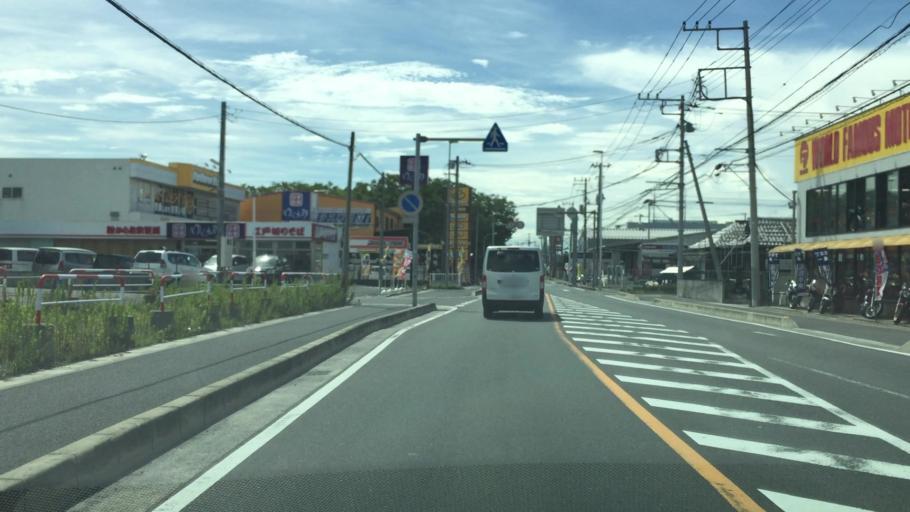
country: JP
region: Saitama
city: Yashio-shi
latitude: 35.8493
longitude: 139.8509
